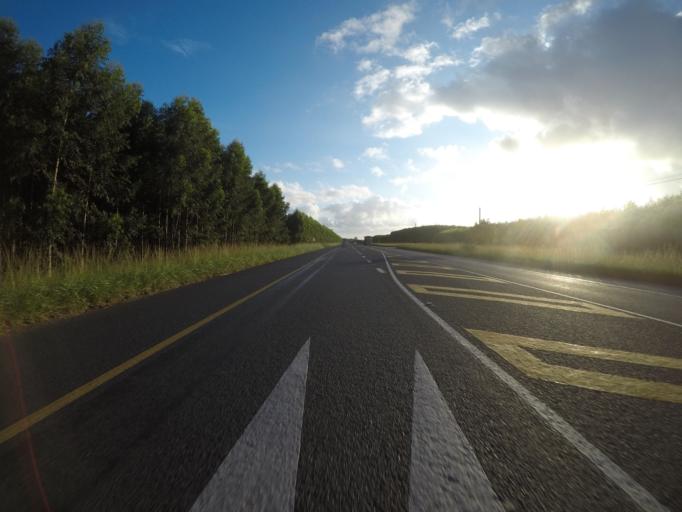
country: ZA
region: KwaZulu-Natal
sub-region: uThungulu District Municipality
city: KwaMbonambi
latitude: -28.6224
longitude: 32.0742
